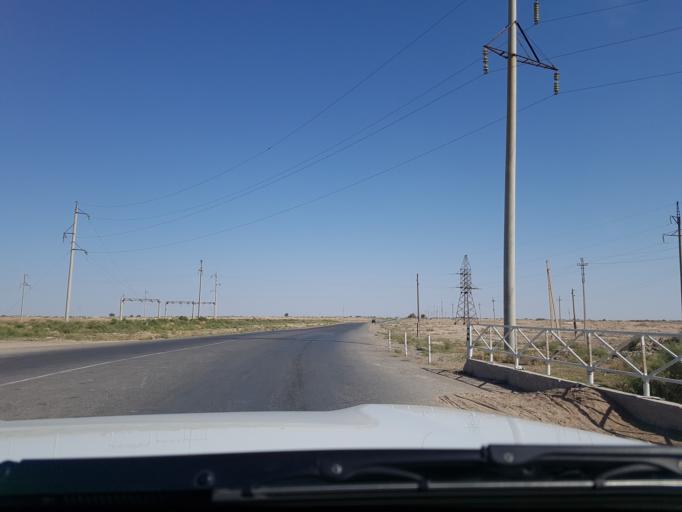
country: IR
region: Razavi Khorasan
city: Sarakhs
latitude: 36.5240
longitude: 61.2365
